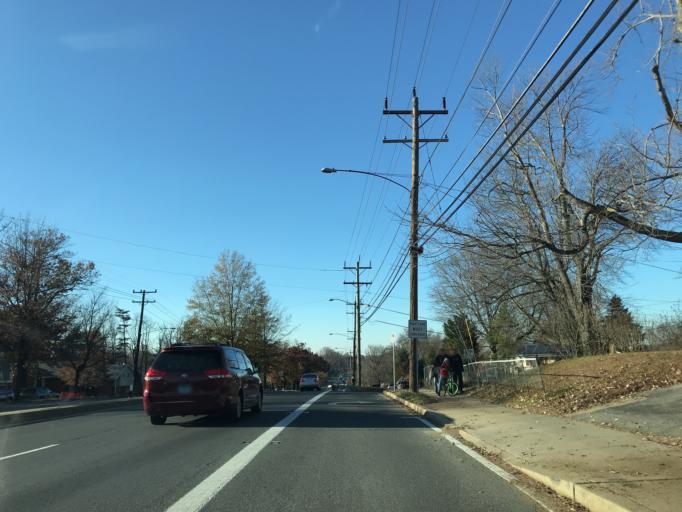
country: US
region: Maryland
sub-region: Montgomery County
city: Wheaton
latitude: 39.0418
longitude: -77.0585
